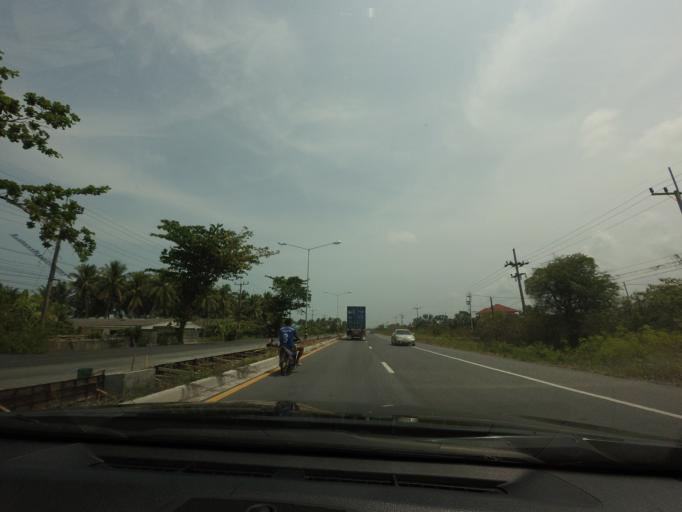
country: TH
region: Nakhon Si Thammarat
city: Hua Sai
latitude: 7.9480
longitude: 100.3321
